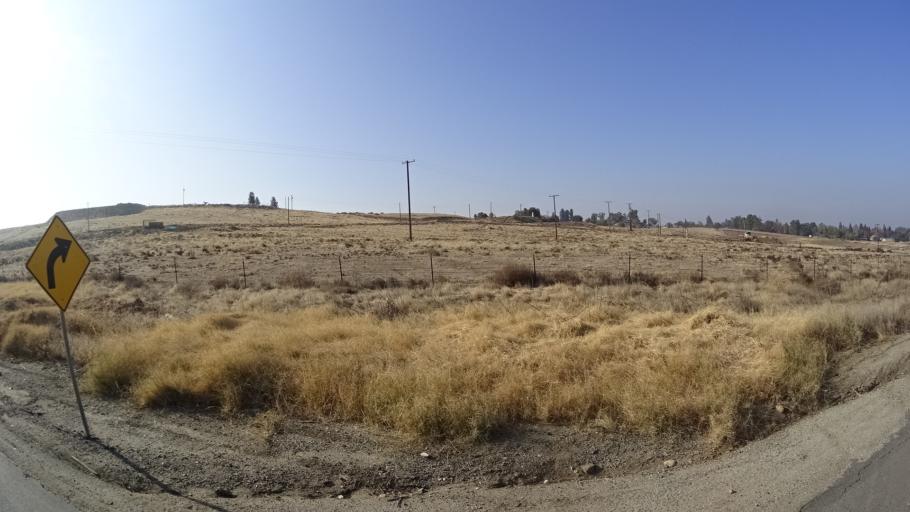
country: US
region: California
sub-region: Kern County
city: Lamont
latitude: 35.4016
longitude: -118.8579
